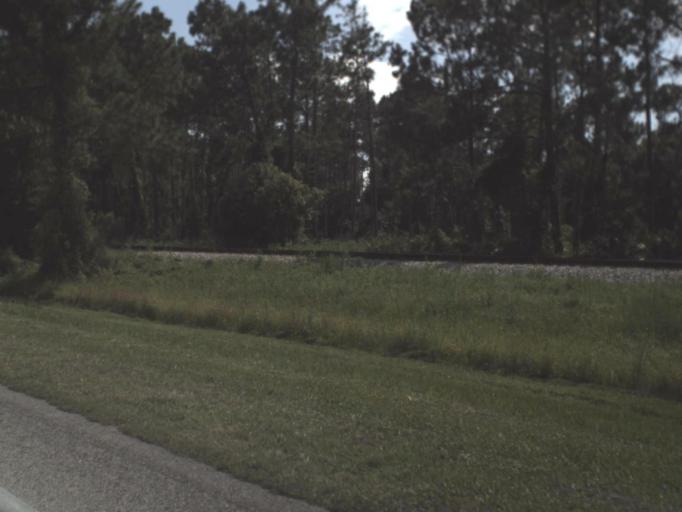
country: US
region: Florida
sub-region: Alachua County
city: Hawthorne
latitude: 29.5403
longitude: -82.1004
